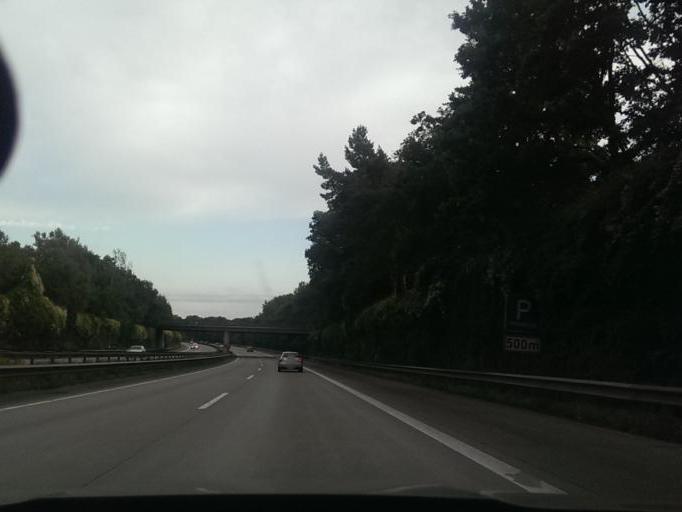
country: DE
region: Lower Saxony
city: Lilienthal
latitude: 53.0981
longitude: 8.8850
